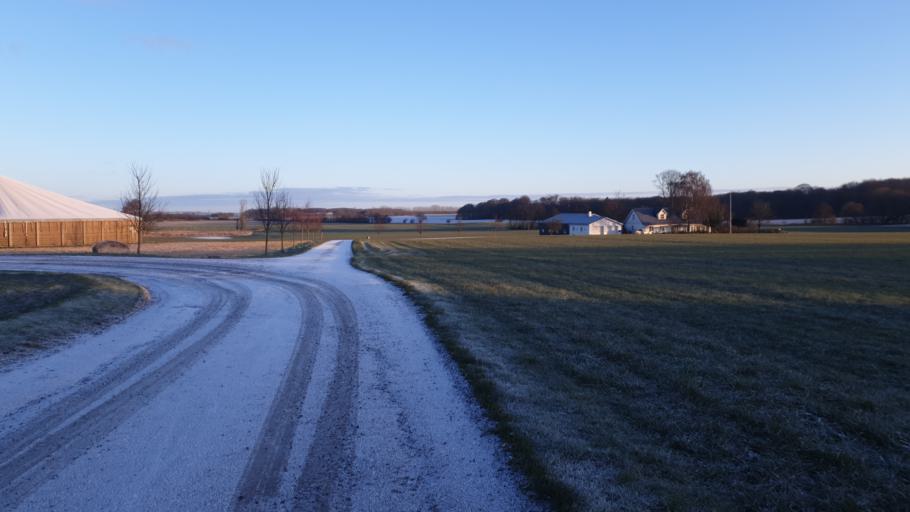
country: DK
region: Central Jutland
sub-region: Hedensted Kommune
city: Hedensted
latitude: 55.8190
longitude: 9.7014
